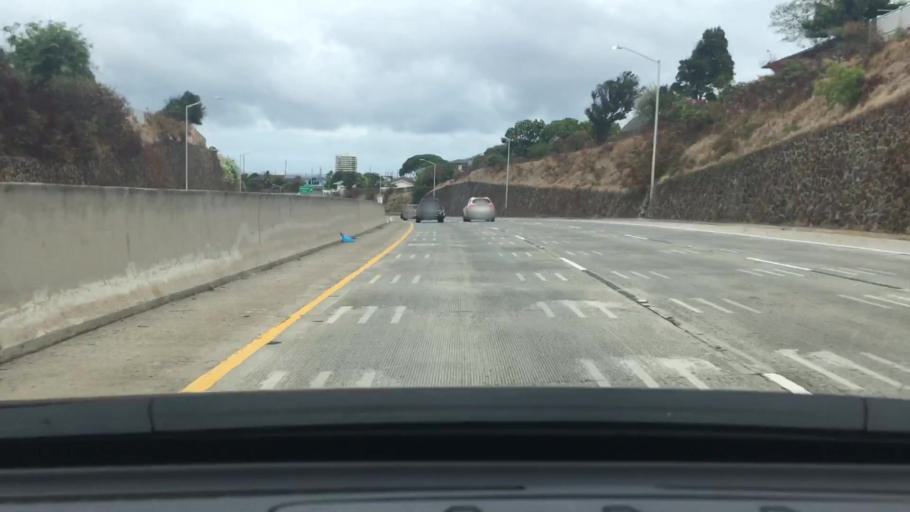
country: US
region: Hawaii
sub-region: Honolulu County
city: Honolulu
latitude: 21.2792
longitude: -157.7981
